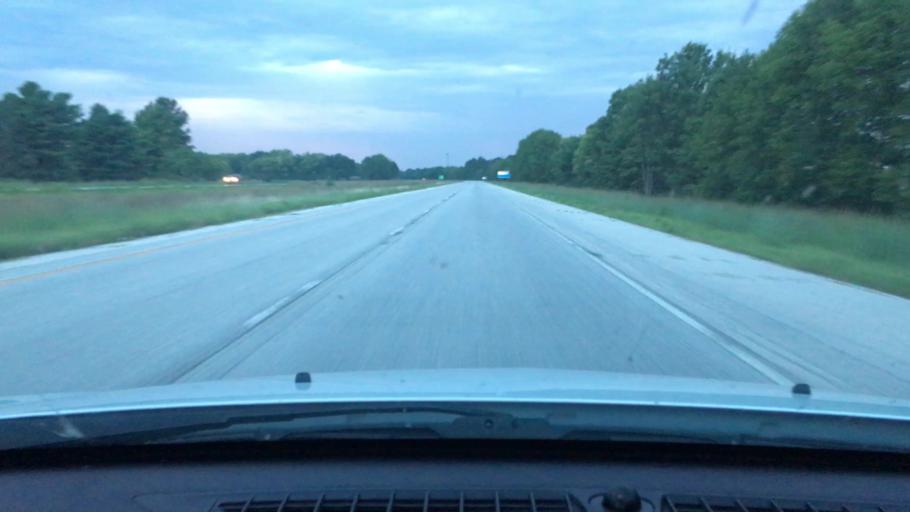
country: US
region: Illinois
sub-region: Morgan County
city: Jacksonville
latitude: 39.7379
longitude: -90.1390
